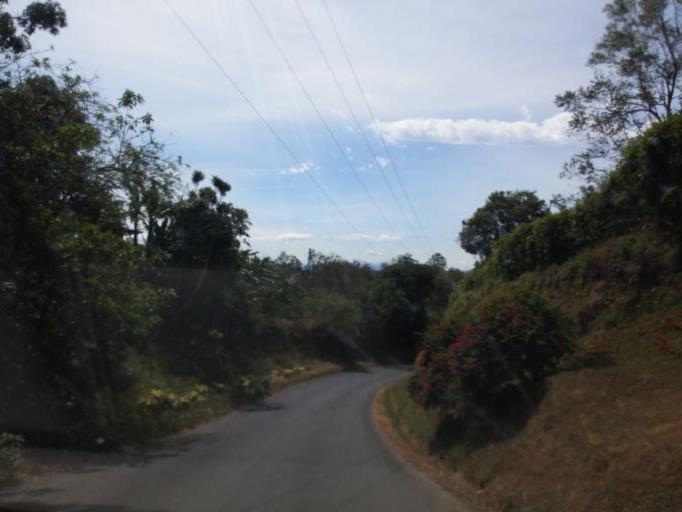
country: CR
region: Alajuela
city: Sabanilla
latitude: 10.0676
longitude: -84.2085
